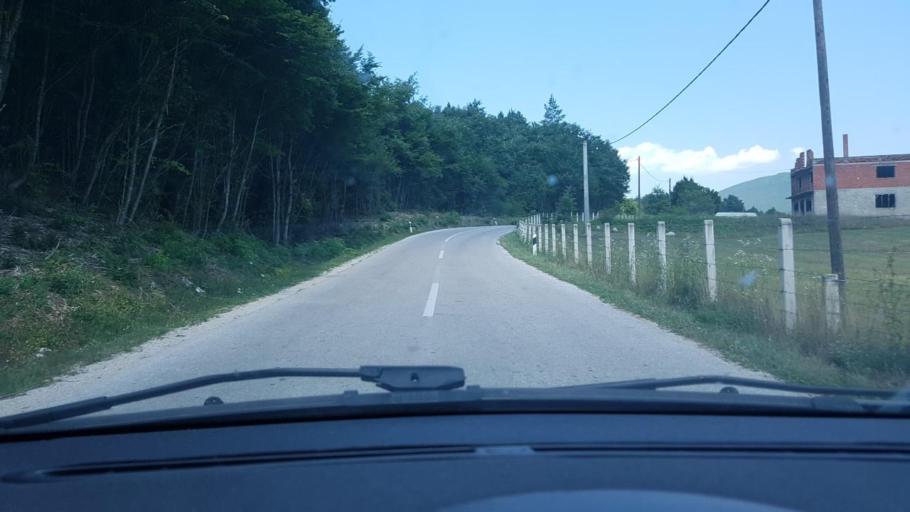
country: BA
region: Federation of Bosnia and Herzegovina
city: Orasac
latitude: 44.6056
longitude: 16.0699
